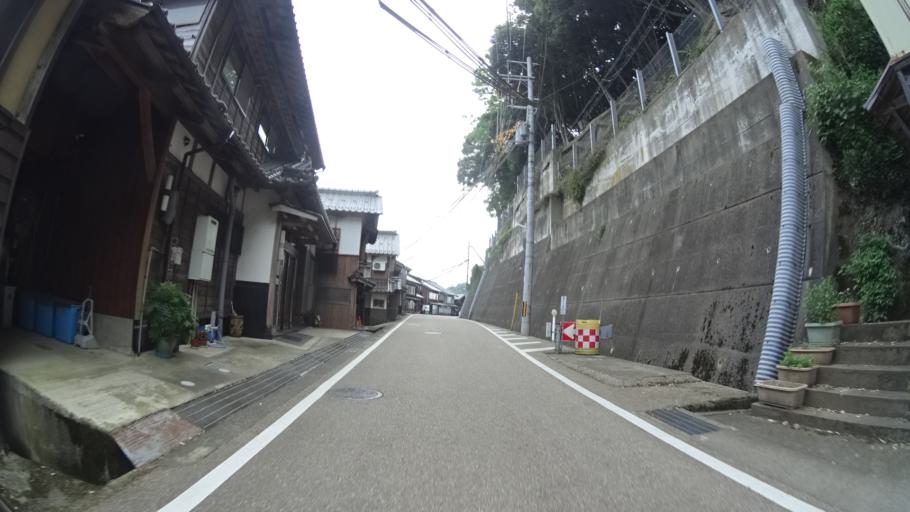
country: JP
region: Kyoto
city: Miyazu
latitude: 35.6705
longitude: 135.2832
